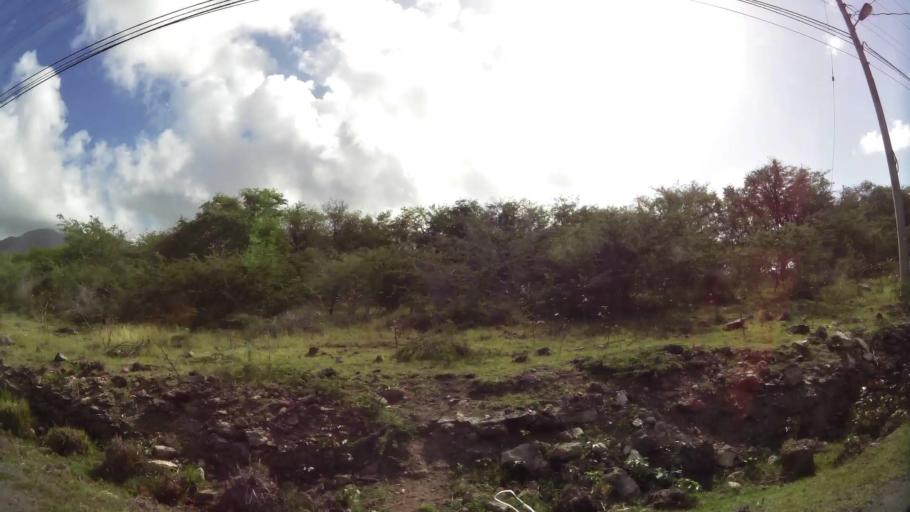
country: KN
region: Saint Paul Charlestown
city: Charlestown
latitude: 17.1223
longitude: -62.6184
